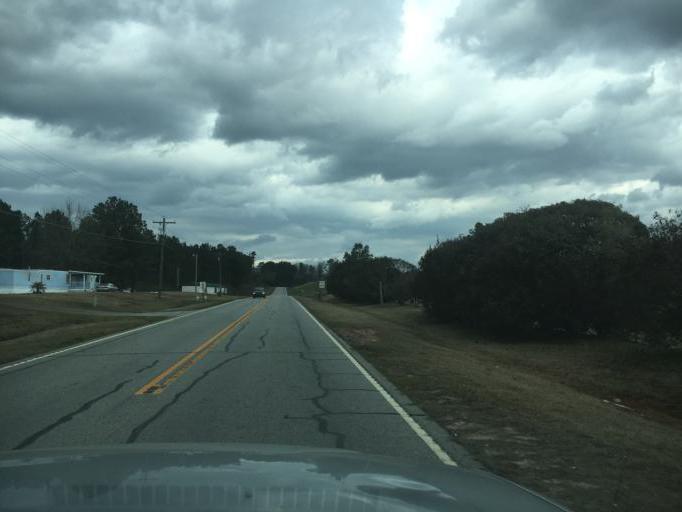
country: US
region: South Carolina
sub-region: Oconee County
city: Westminster
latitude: 34.6922
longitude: -83.0809
